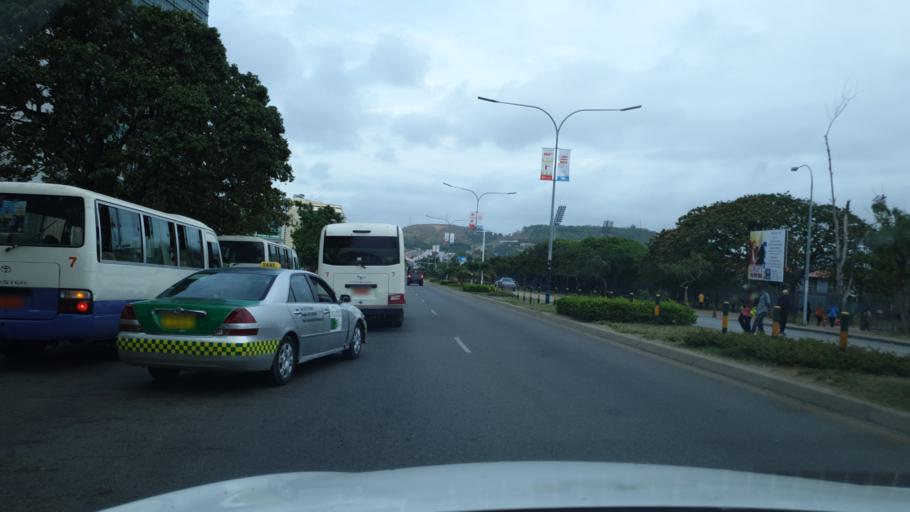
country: PG
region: National Capital
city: Port Moresby
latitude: -9.4390
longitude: 147.1816
